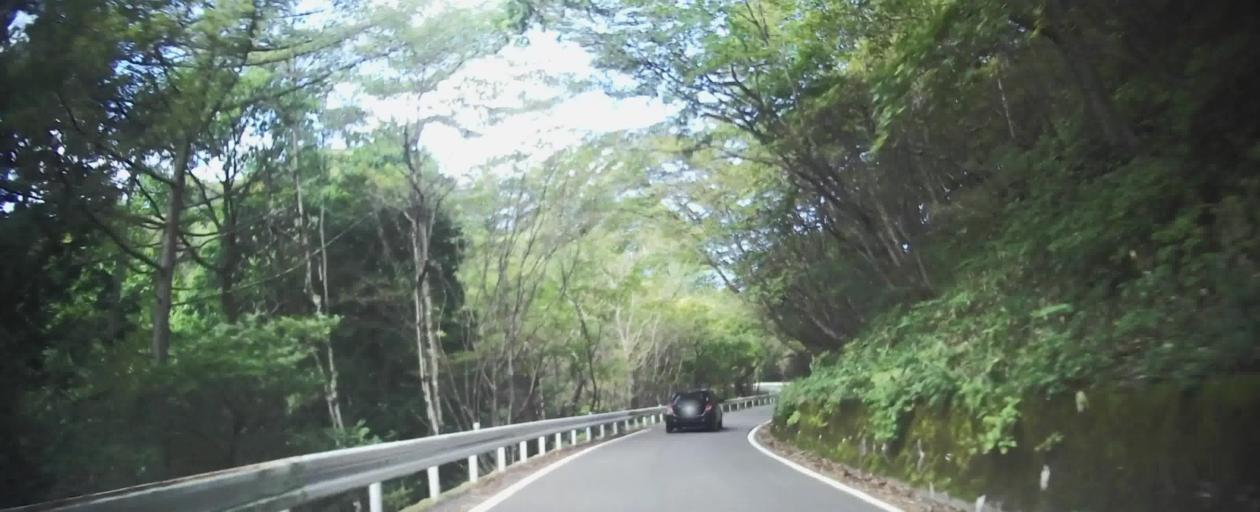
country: JP
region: Gunma
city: Shibukawa
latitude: 36.4642
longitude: 138.8894
